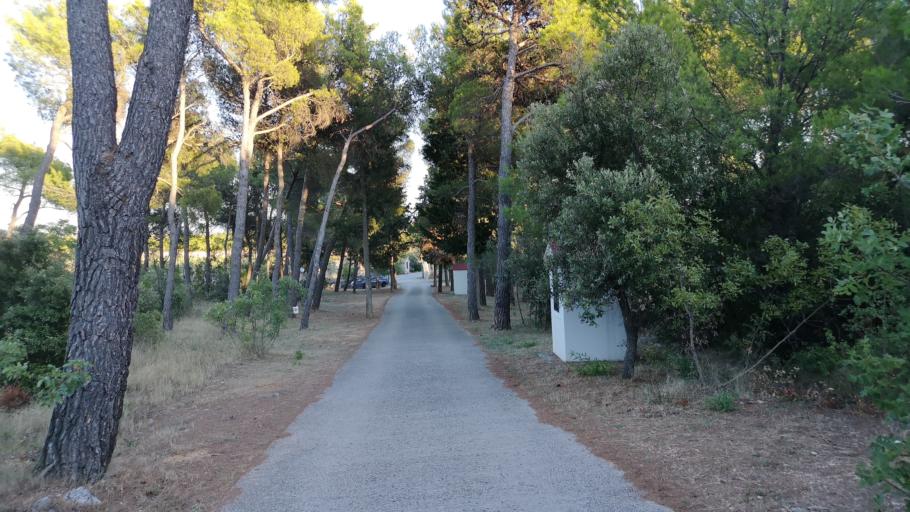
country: HR
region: Sibensko-Kniniska
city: Vodice
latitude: 43.7844
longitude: 15.7718
